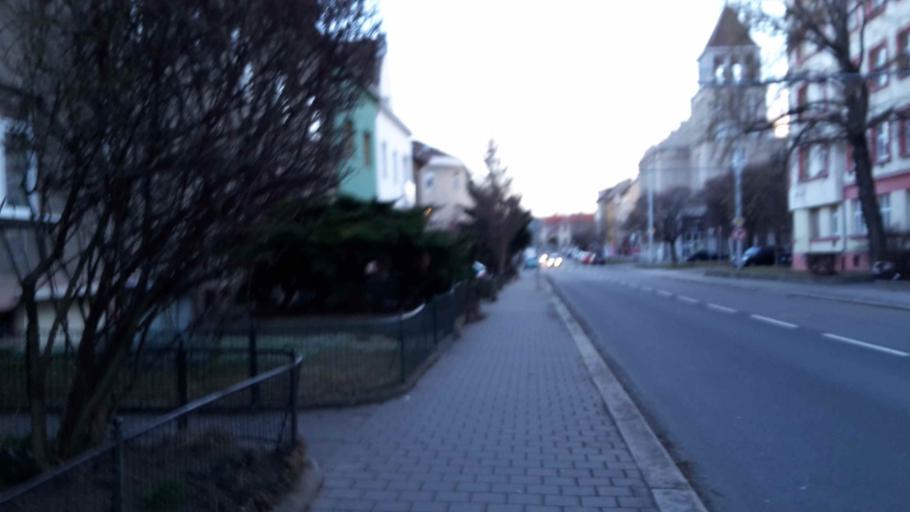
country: CZ
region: South Moravian
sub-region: Mesto Brno
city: Brno
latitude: 49.2223
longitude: 16.5917
